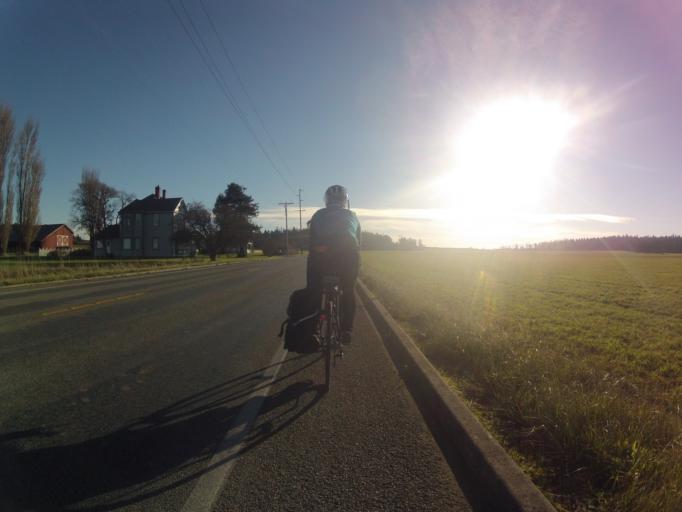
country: US
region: Washington
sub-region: Island County
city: Coupeville
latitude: 48.1962
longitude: -122.6863
